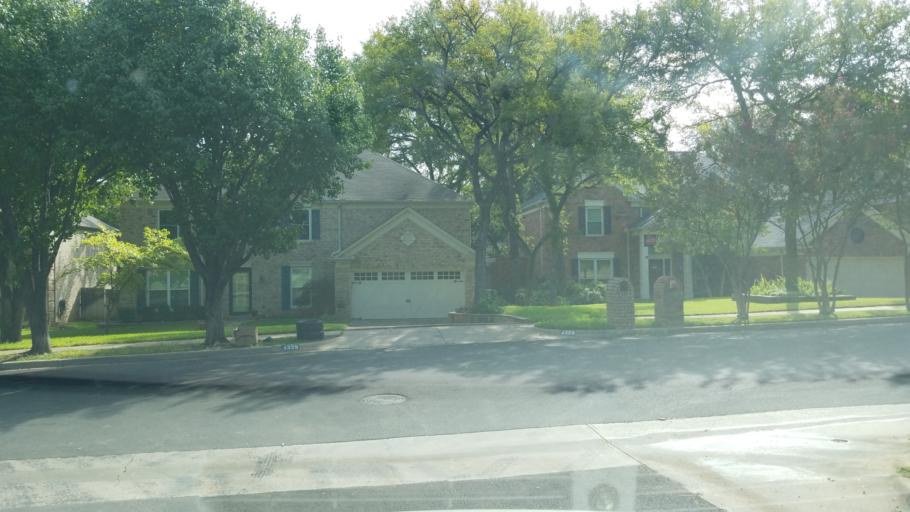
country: US
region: Texas
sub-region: Tarrant County
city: Grapevine
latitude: 32.8910
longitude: -97.0891
